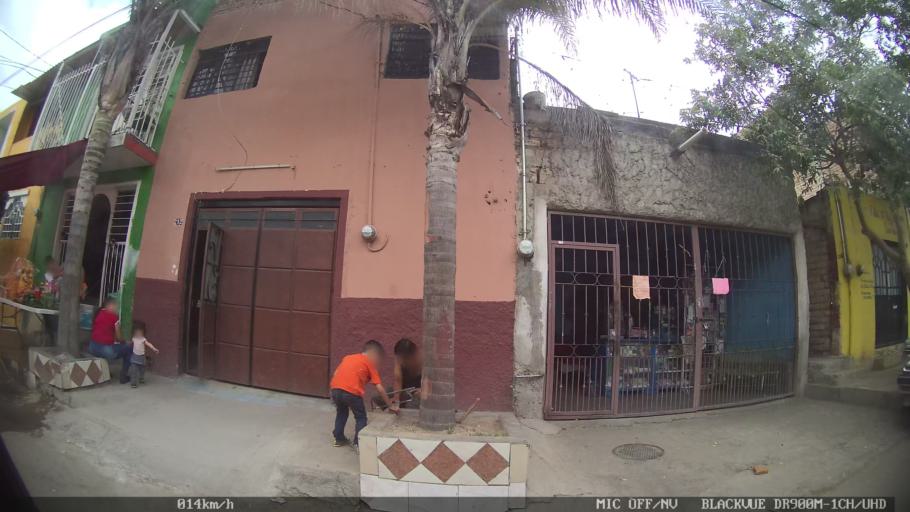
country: MX
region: Jalisco
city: Tlaquepaque
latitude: 20.6541
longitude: -103.2652
